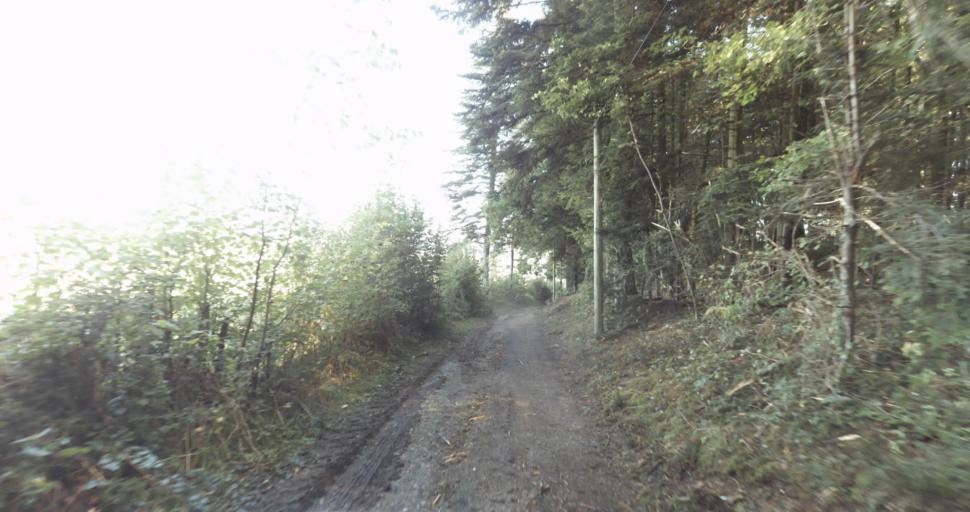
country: FR
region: Lower Normandy
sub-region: Departement de l'Orne
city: Vimoutiers
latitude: 48.9313
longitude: 0.2947
